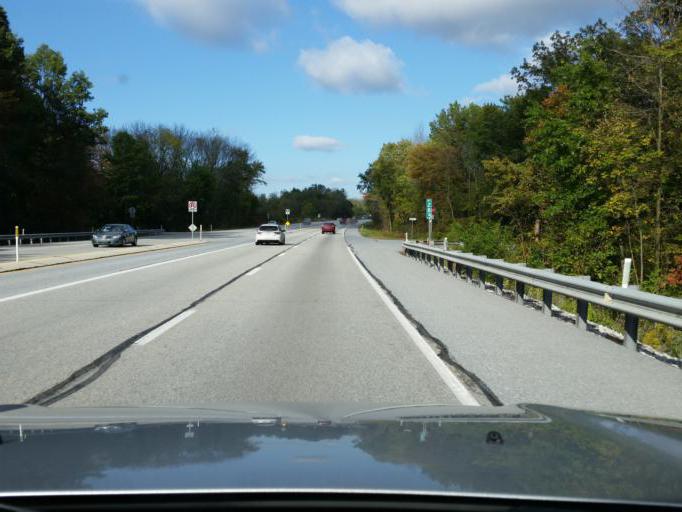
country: US
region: Pennsylvania
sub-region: York County
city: Dillsburg
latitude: 40.0629
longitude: -77.0642
